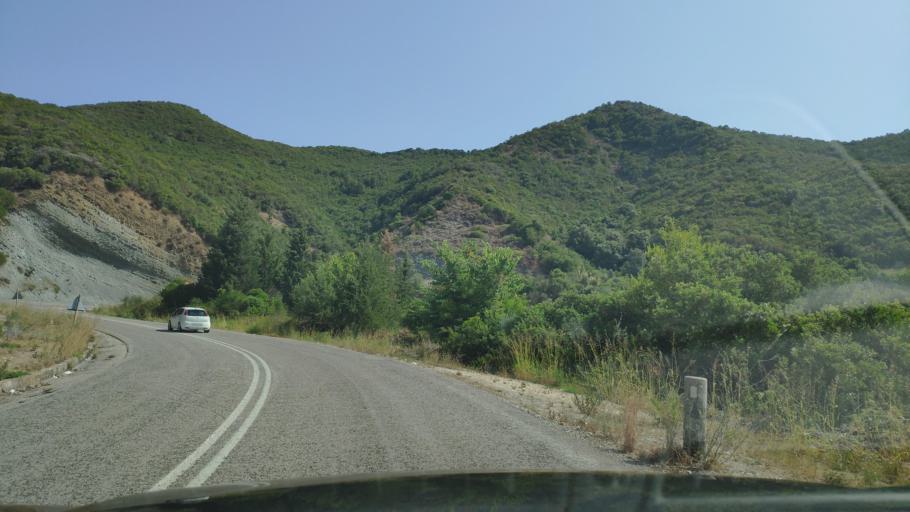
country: GR
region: Epirus
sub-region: Nomos Artas
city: Peta
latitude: 39.1692
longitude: 21.0611
